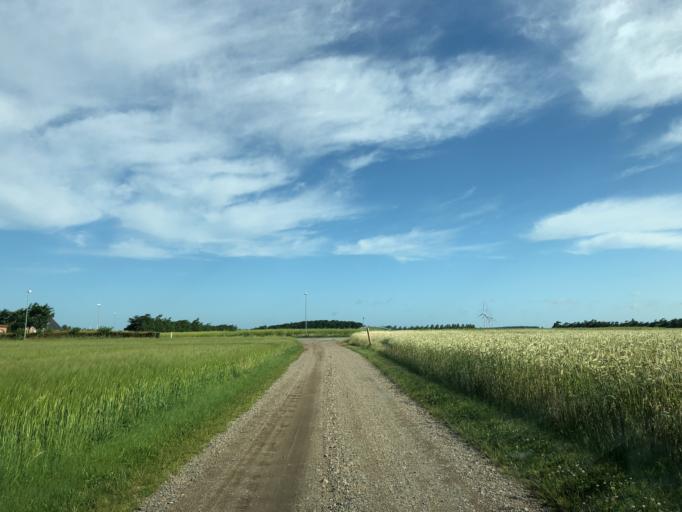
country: DK
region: Central Jutland
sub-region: Holstebro Kommune
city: Ulfborg
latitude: 56.3383
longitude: 8.3081
